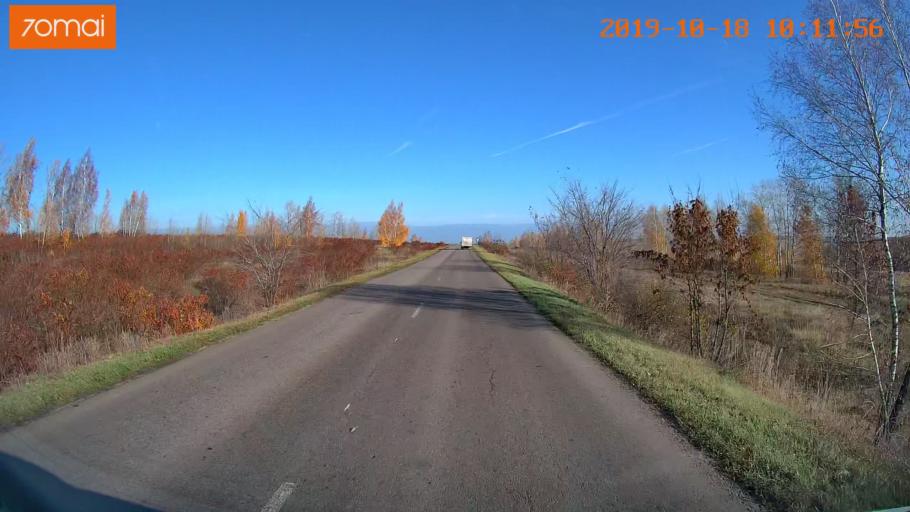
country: RU
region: Tula
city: Kurkino
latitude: 53.3880
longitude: 38.5038
